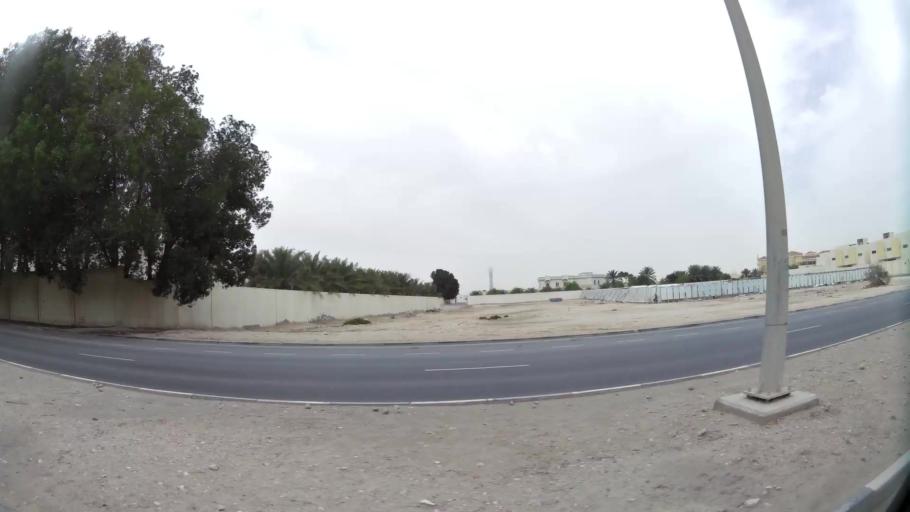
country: QA
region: Baladiyat ad Dawhah
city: Doha
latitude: 25.2340
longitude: 51.4675
